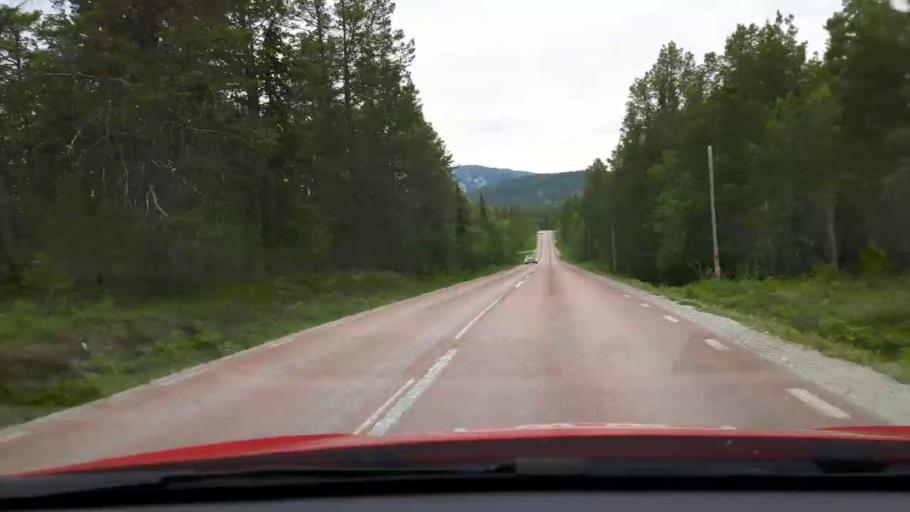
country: NO
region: Hedmark
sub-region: Engerdal
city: Engerdal
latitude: 62.5106
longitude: 12.6083
